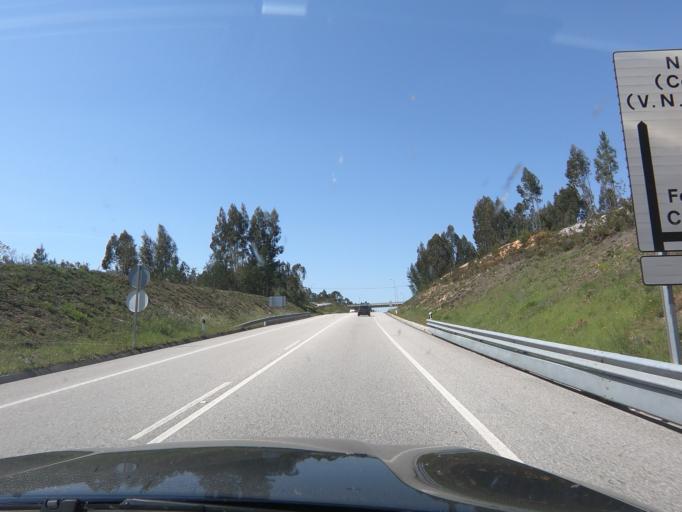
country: PT
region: Coimbra
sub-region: Lousa
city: Lousa
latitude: 40.1620
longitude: -8.2634
